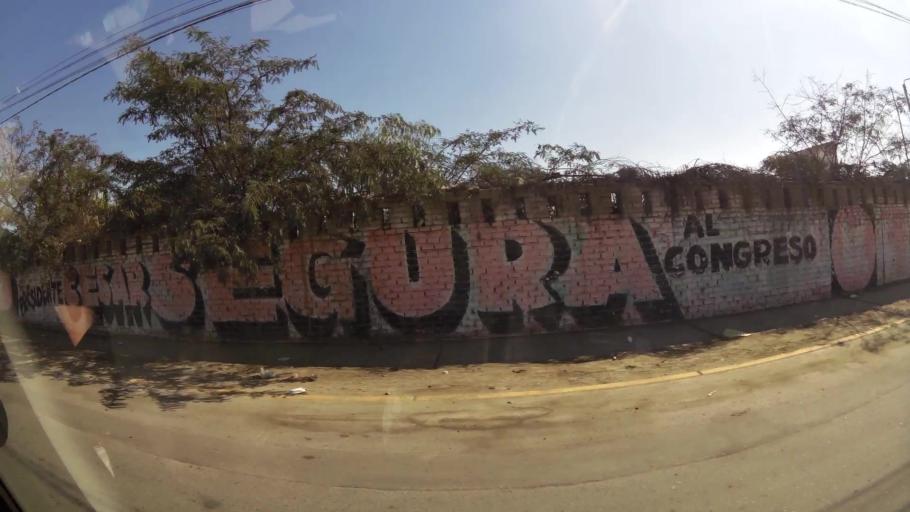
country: PE
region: Ica
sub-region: Provincia de Ica
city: La Tinguina
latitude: -14.0371
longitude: -75.7010
